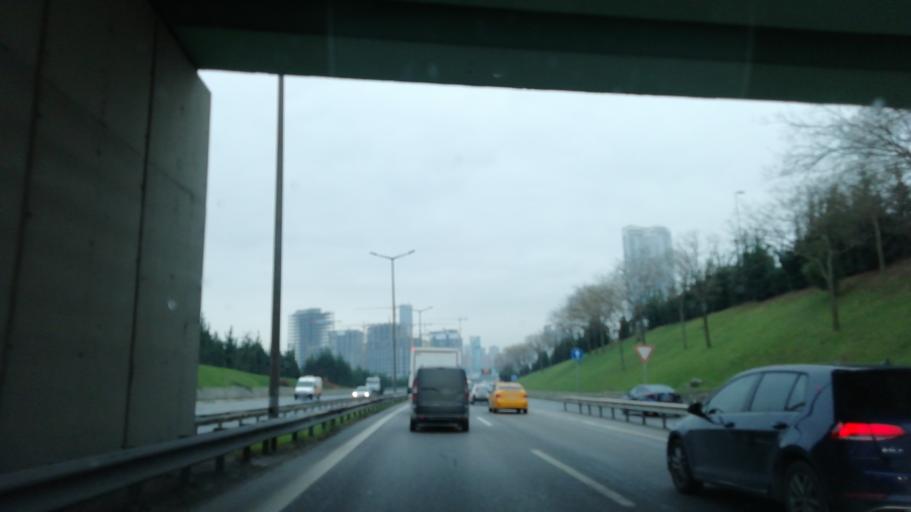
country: TR
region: Istanbul
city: Umraniye
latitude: 41.0072
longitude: 29.0972
